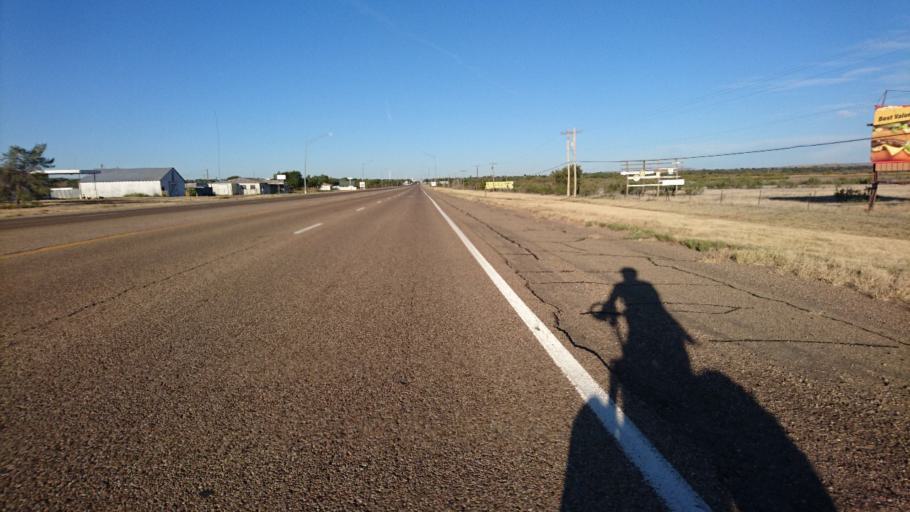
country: US
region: New Mexico
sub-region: Quay County
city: Tucumcari
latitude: 35.1720
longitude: -103.6896
